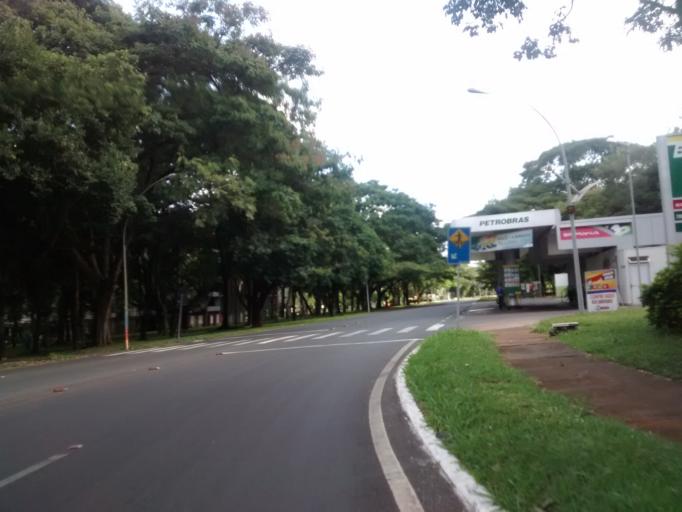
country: BR
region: Federal District
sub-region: Brasilia
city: Brasilia
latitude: -15.8086
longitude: -47.8964
